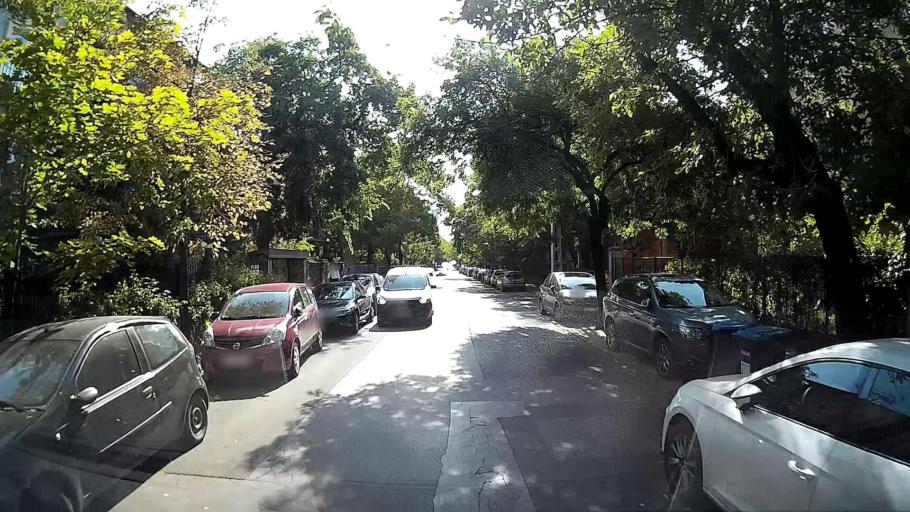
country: HU
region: Budapest
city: Budapest XIV. keruelet
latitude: 47.5200
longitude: 19.0949
